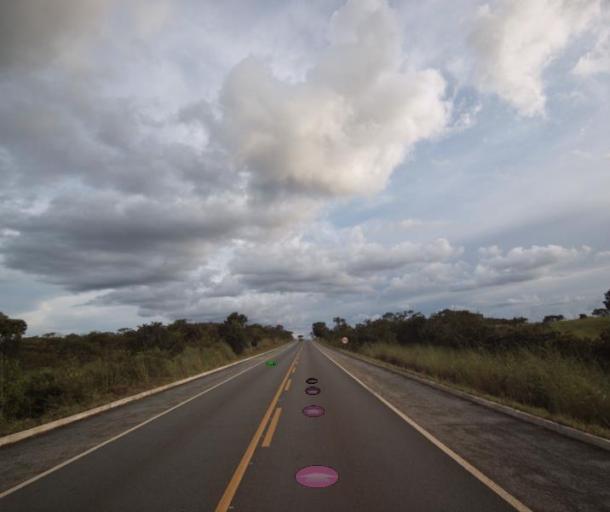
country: BR
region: Goias
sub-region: Barro Alto
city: Barro Alto
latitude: -14.8896
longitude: -48.6411
